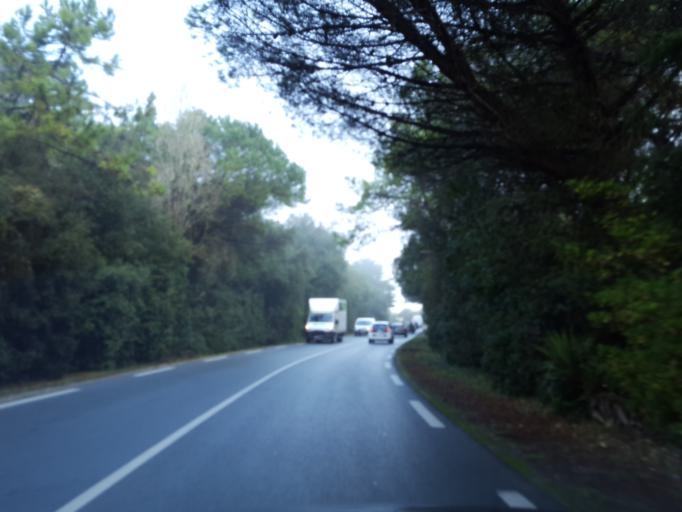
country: FR
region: Poitou-Charentes
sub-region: Departement de la Charente-Maritime
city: La Flotte
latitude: 46.1908
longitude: -1.3463
